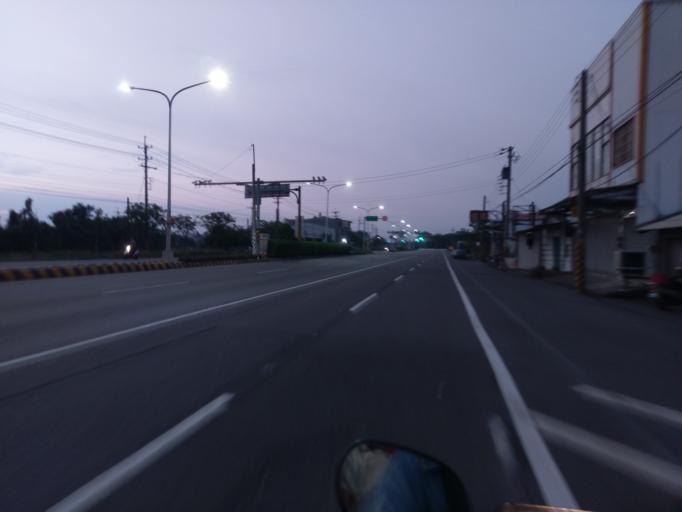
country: TW
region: Taiwan
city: Xinying
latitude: 23.1926
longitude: 120.3249
